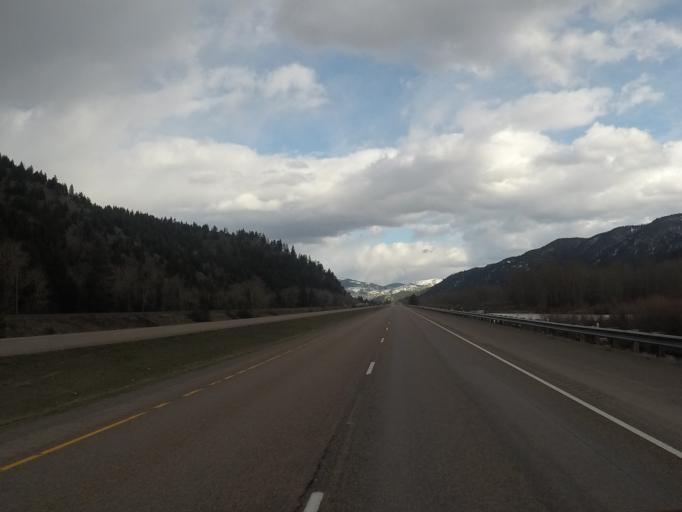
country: US
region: Montana
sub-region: Missoula County
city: Clinton
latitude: 46.8198
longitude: -113.8011
